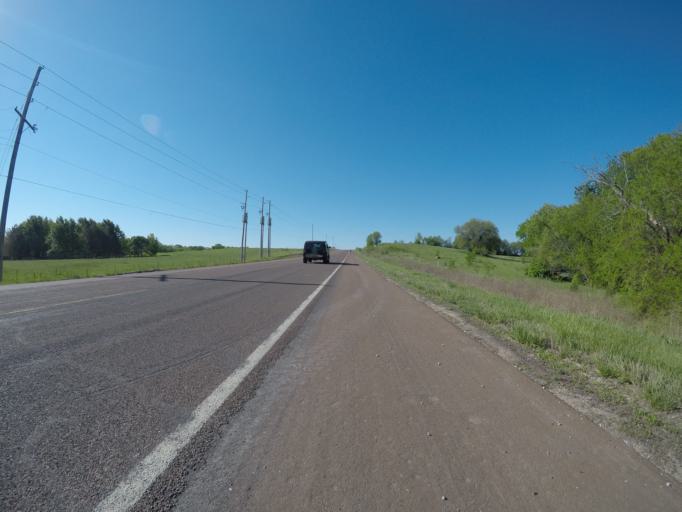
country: US
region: Kansas
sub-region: Douglas County
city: Lawrence
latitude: 39.0343
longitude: -95.3913
